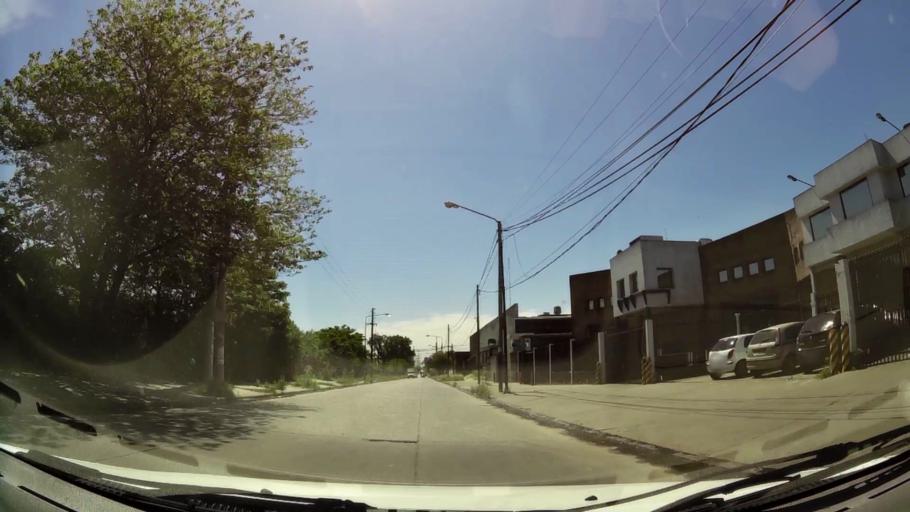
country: AR
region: Buenos Aires
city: Caseros
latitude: -34.5647
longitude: -58.5798
